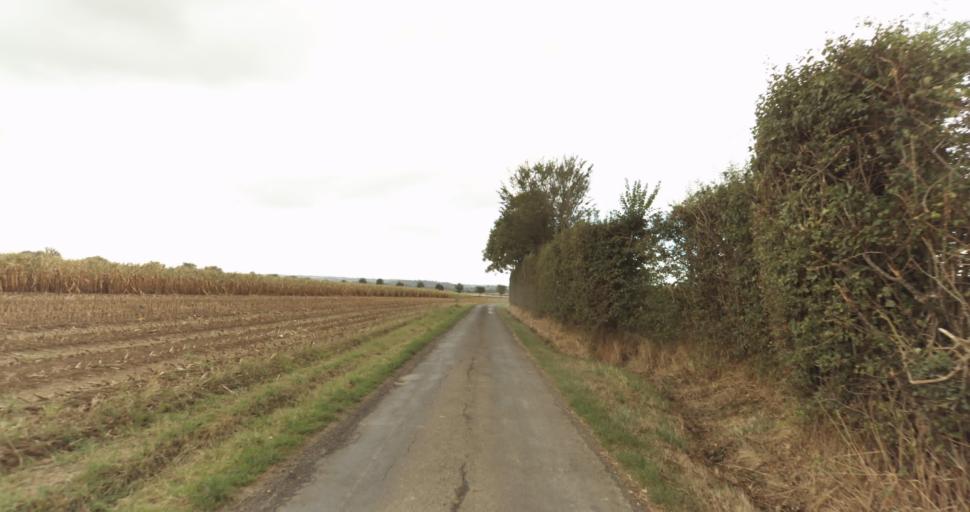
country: FR
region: Lower Normandy
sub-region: Departement de l'Orne
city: Gace
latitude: 48.6951
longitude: 0.2500
